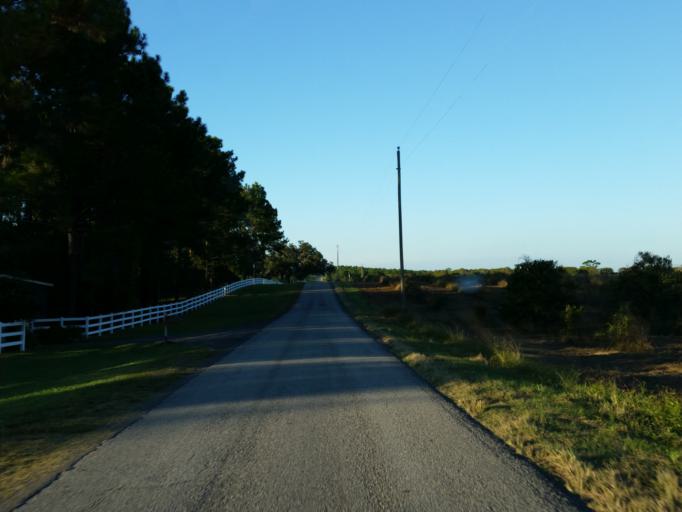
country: US
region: Florida
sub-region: Pasco County
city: Dade City North
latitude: 28.4326
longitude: -82.2698
